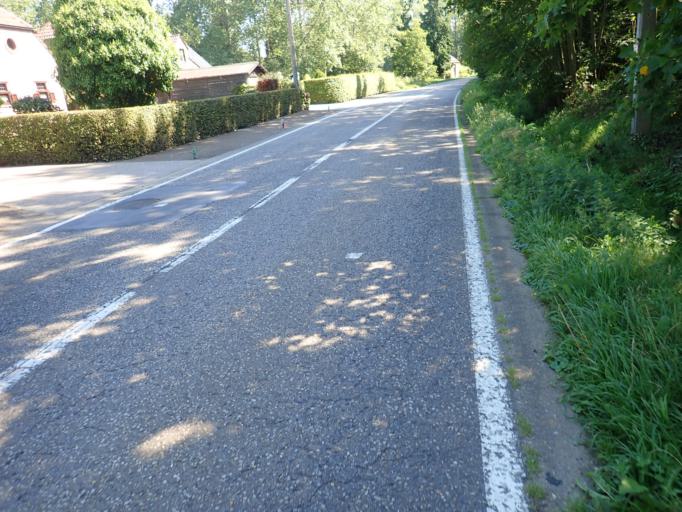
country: BE
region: Flanders
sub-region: Provincie Antwerpen
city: Herselt
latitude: 51.0542
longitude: 4.8497
